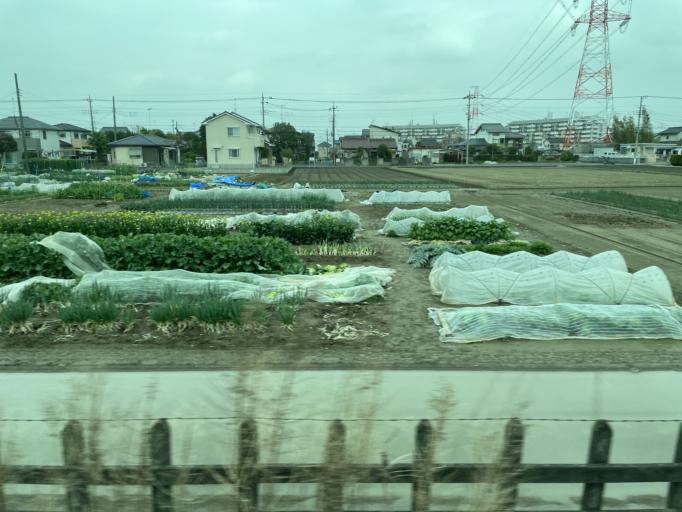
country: JP
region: Saitama
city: Sugito
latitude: 36.0309
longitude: 139.7156
